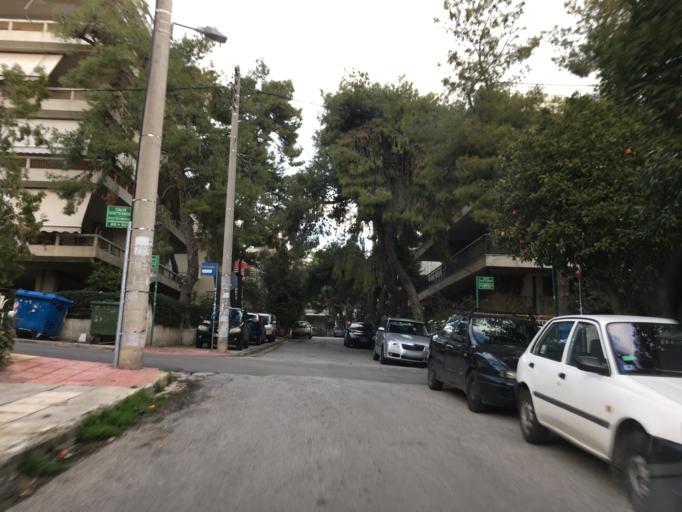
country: GR
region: Attica
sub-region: Nomarchia Athinas
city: Irakleio
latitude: 38.0455
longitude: 23.7724
